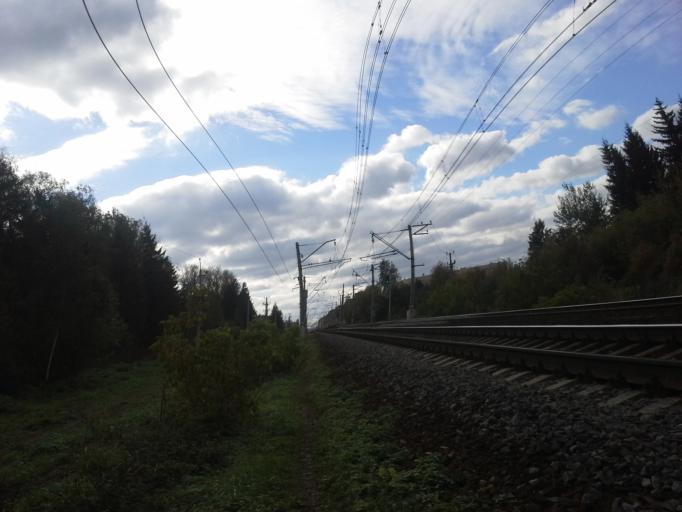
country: RU
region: Moskovskaya
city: Krasnoznamensk
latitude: 55.6284
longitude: 37.0372
